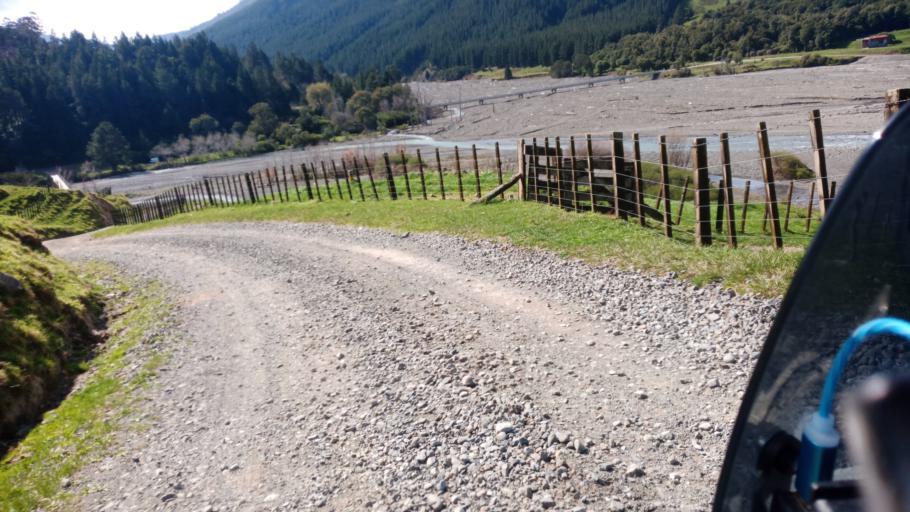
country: NZ
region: Gisborne
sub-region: Gisborne District
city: Gisborne
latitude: -37.8560
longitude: 178.0882
